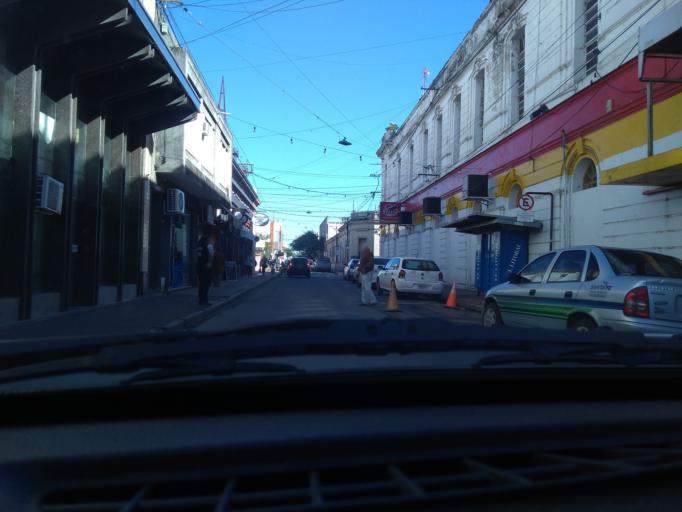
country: AR
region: Santa Fe
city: Santa Fe de la Vera Cruz
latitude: -31.6513
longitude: -60.7088
